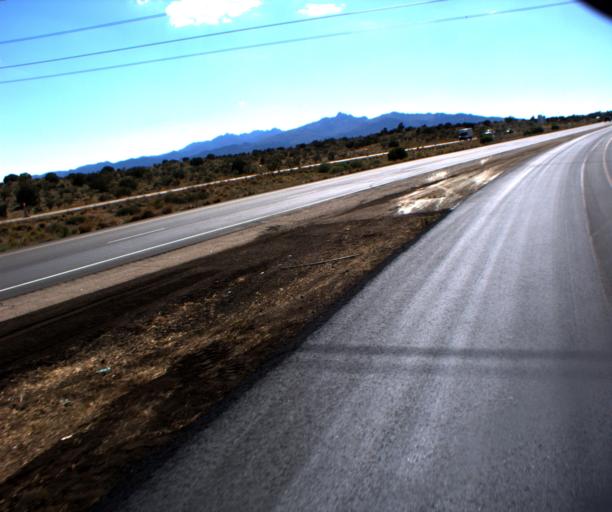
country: US
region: Arizona
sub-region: Mohave County
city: New Kingman-Butler
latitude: 35.1605
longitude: -113.7040
